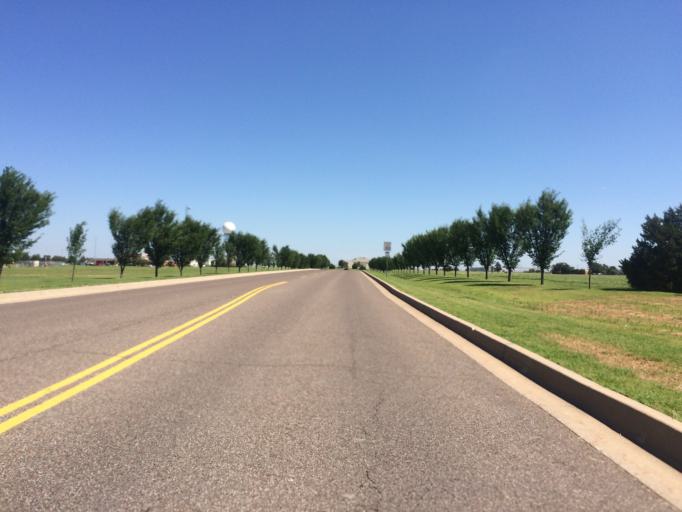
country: US
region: Oklahoma
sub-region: Cleveland County
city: Norman
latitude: 35.2334
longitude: -97.4590
